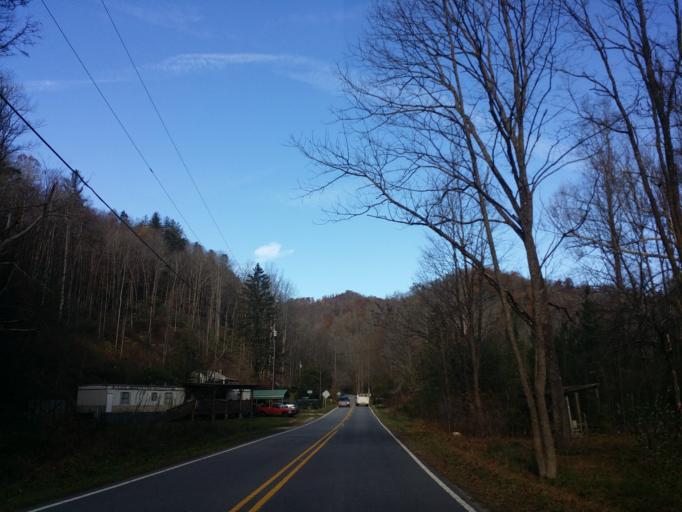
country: US
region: North Carolina
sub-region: McDowell County
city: West Marion
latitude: 35.7357
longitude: -82.1300
